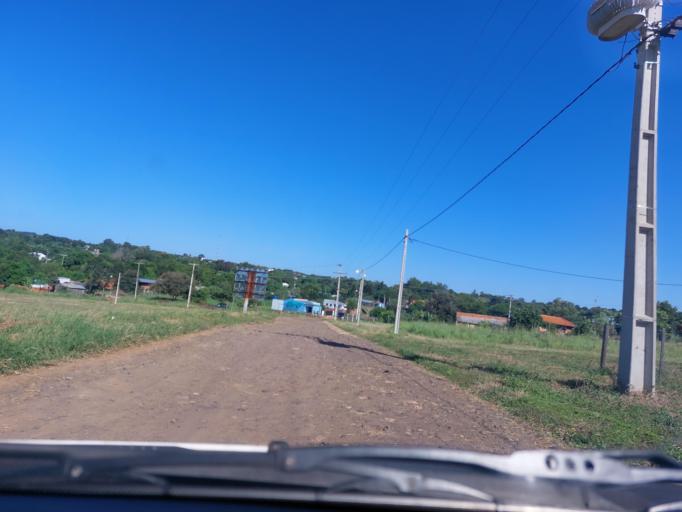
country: PY
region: San Pedro
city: Guayaybi
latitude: -24.6537
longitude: -56.4489
